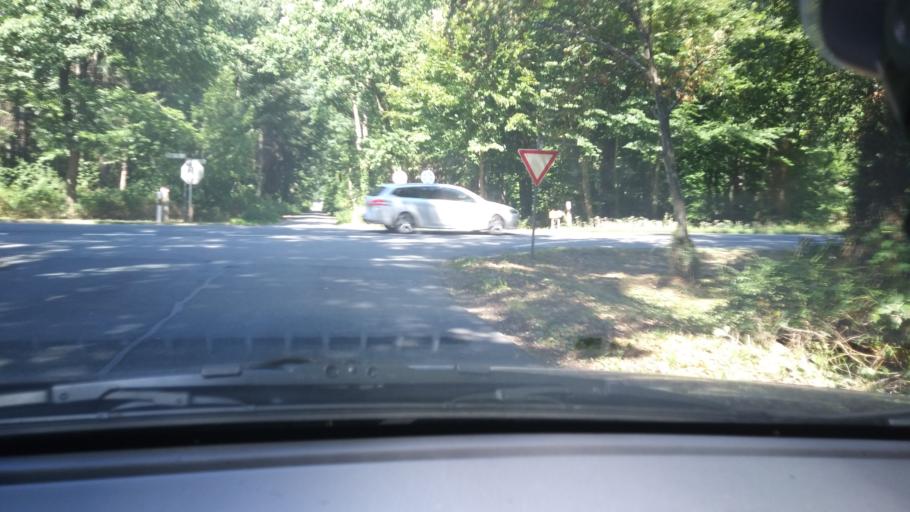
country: DE
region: Lower Saxony
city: Binnen
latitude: 52.6221
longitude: 9.1224
